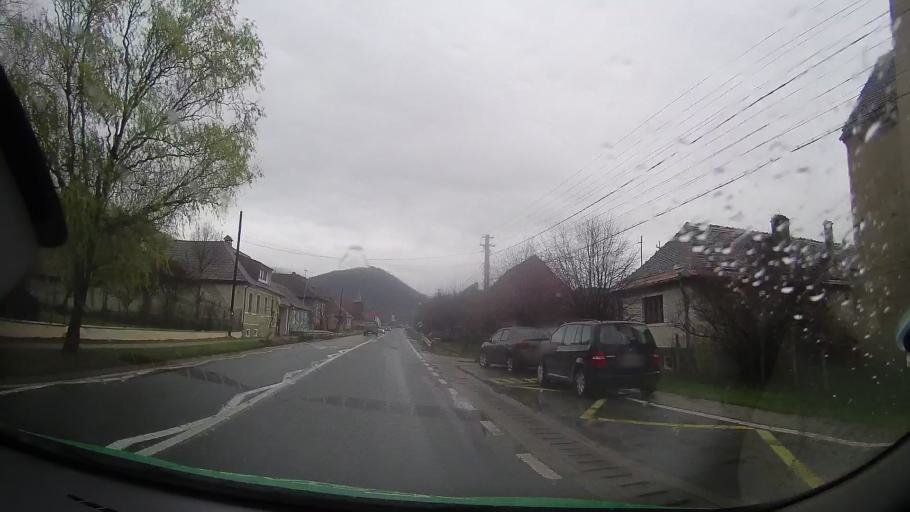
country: RO
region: Bistrita-Nasaud
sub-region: Comuna Teaca
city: Teaca
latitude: 46.9462
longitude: 24.4596
